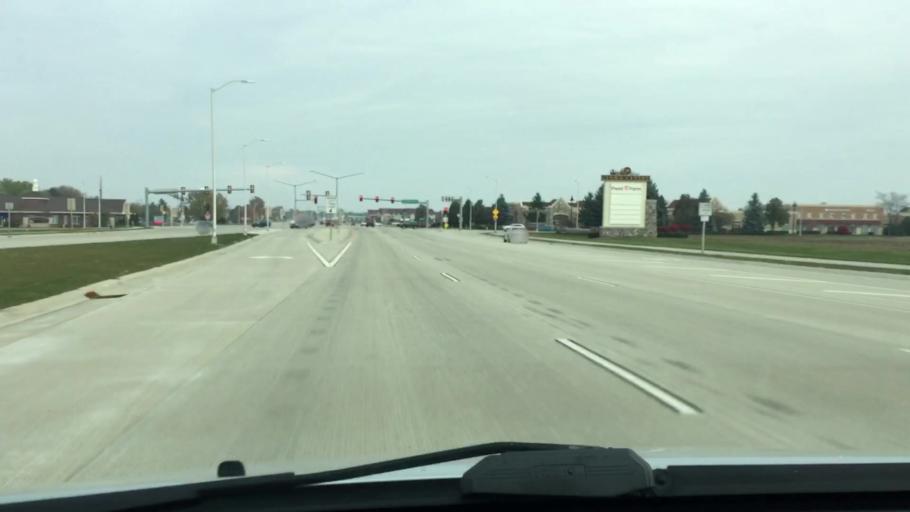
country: US
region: Wisconsin
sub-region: Waukesha County
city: Oconomowoc
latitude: 43.0724
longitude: -88.4709
